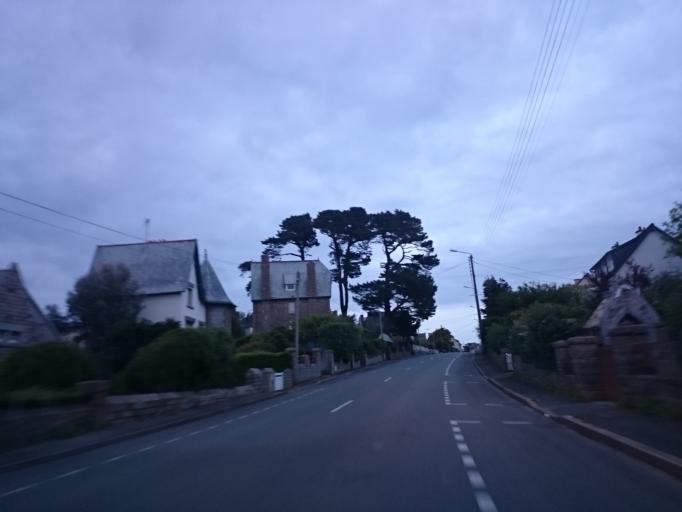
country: FR
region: Brittany
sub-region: Departement des Cotes-d'Armor
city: Perros-Guirec
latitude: 48.8128
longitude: -3.4570
